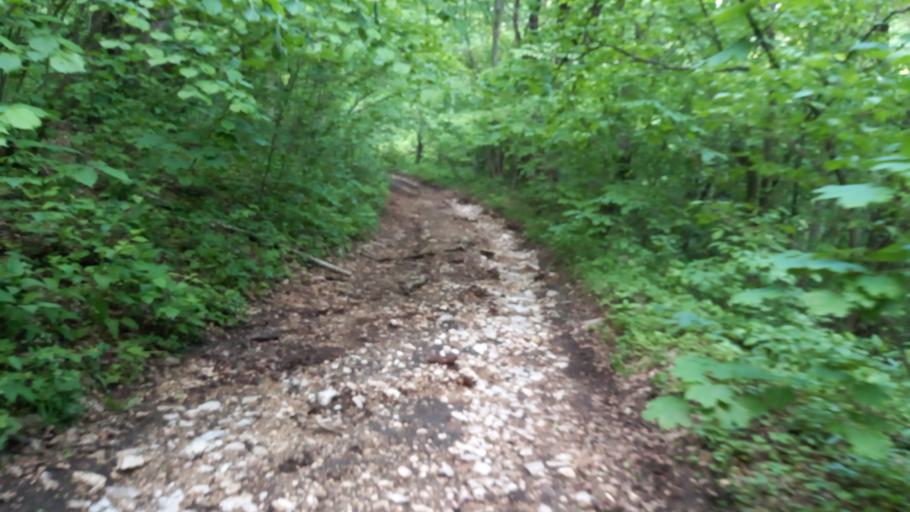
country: RU
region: Adygeya
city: Kamennomostskiy
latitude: 44.2212
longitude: 40.0064
